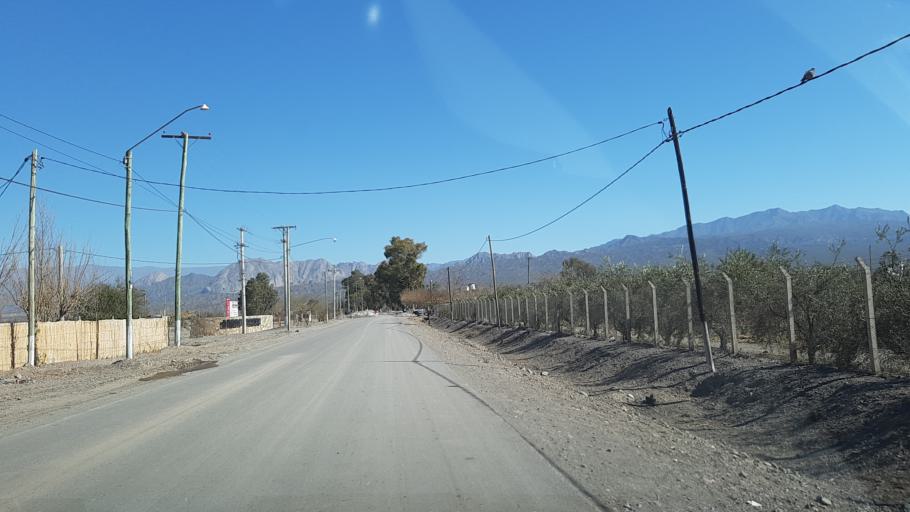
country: AR
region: San Juan
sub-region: Departamento de Zonda
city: Zonda
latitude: -31.4693
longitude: -68.7315
